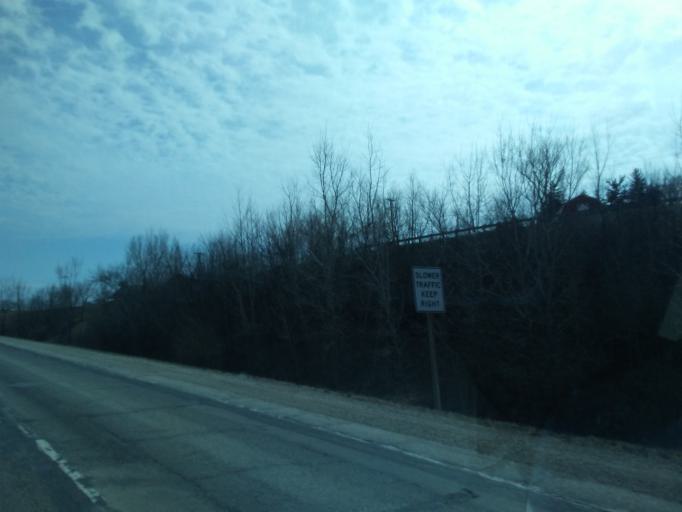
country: US
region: Iowa
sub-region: Winneshiek County
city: Decorah
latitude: 43.2790
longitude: -91.7406
